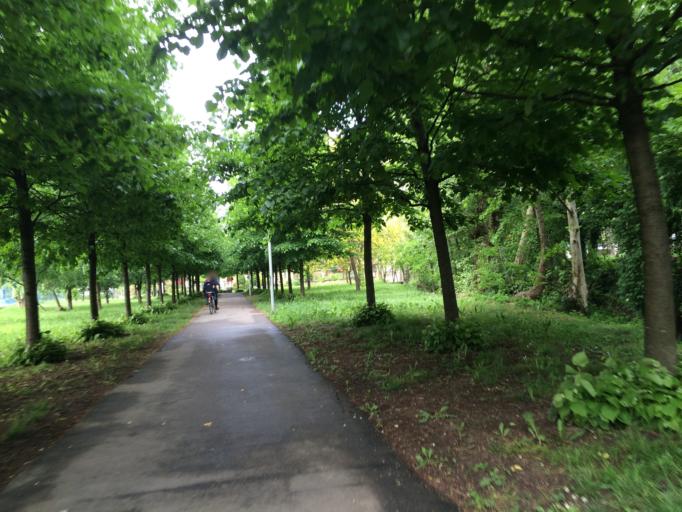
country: IT
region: Lombardy
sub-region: Provincia di Brescia
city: Flero
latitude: 45.4813
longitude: 10.1747
